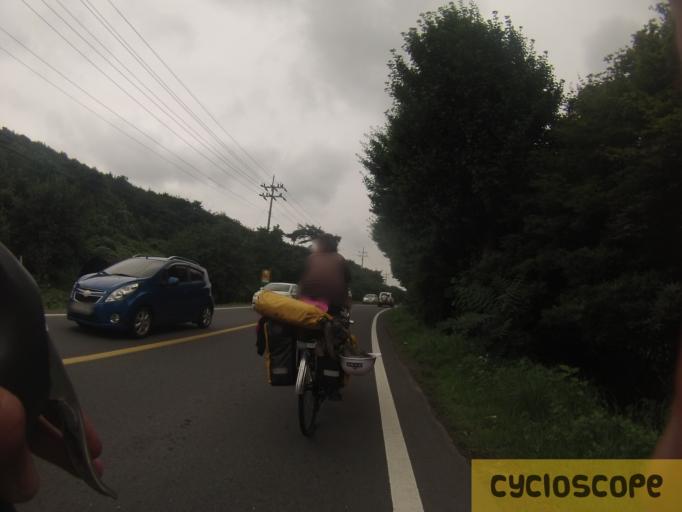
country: KR
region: Chungcheongnam-do
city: Taisen-ri
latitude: 36.4356
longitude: 126.7190
